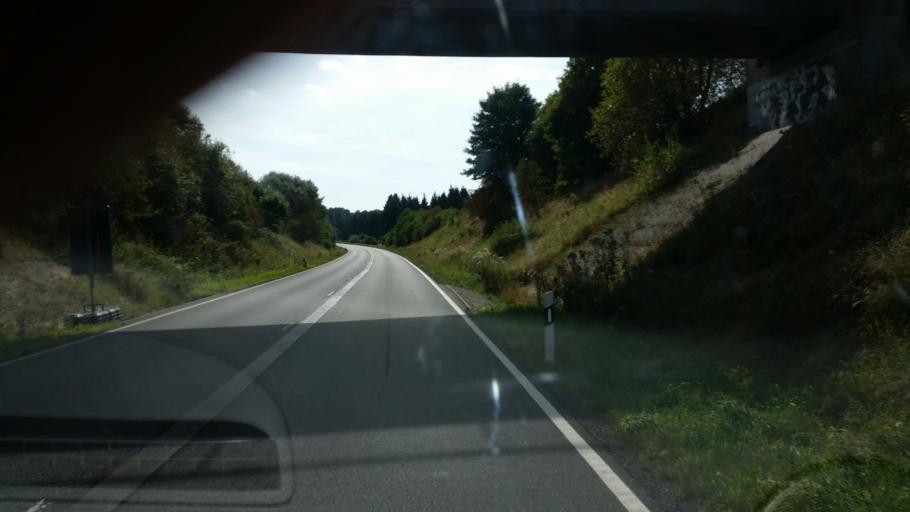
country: DE
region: Rheinland-Pfalz
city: Rennerod
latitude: 50.6238
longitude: 8.0708
